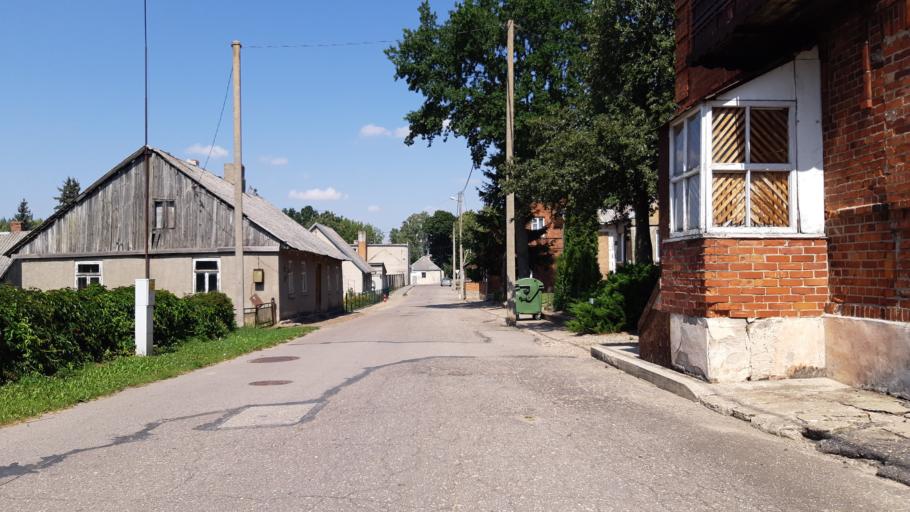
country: LT
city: Virbalis
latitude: 54.6245
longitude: 22.8212
